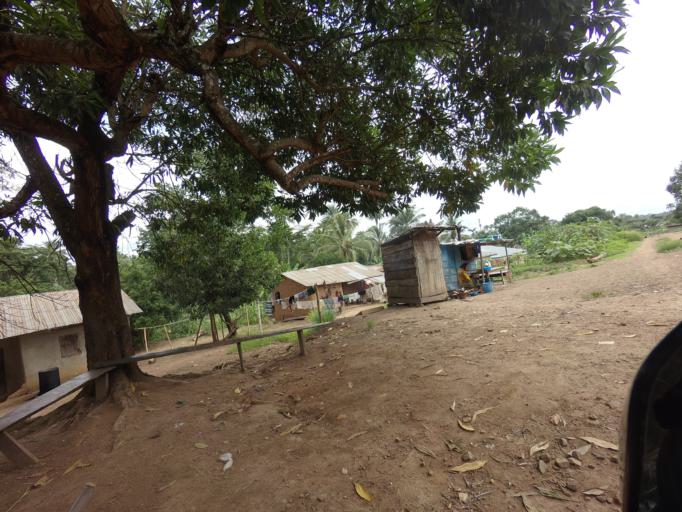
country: SL
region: Eastern Province
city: Tombodu
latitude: 8.1655
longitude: -10.6185
